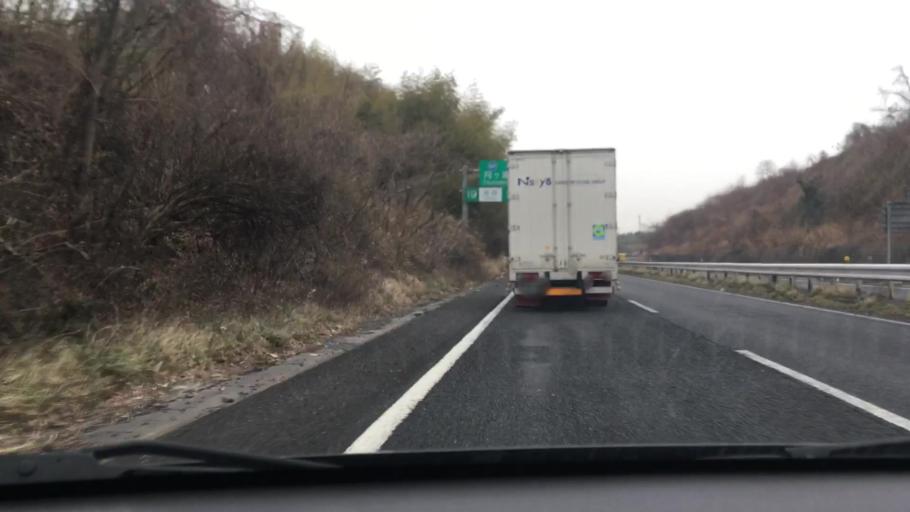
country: JP
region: Mie
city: Nabari
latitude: 34.6995
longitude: 136.0635
